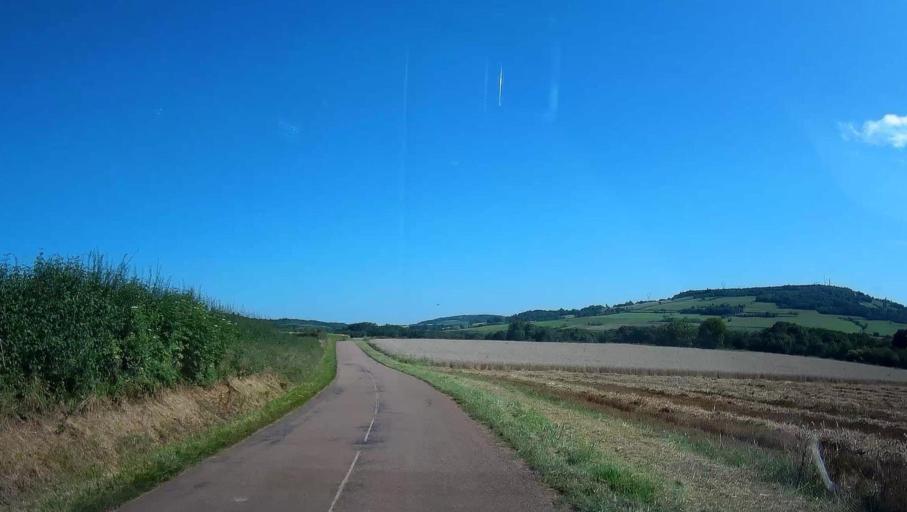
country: FR
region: Bourgogne
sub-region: Departement de Saone-et-Loire
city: Couches
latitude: 46.8922
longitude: 4.5914
